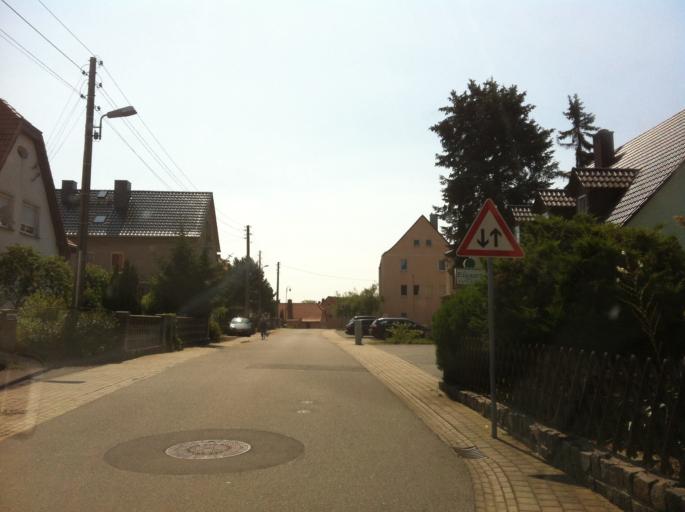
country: DE
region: Saxony
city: Trebsen
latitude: 51.2858
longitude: 12.7613
